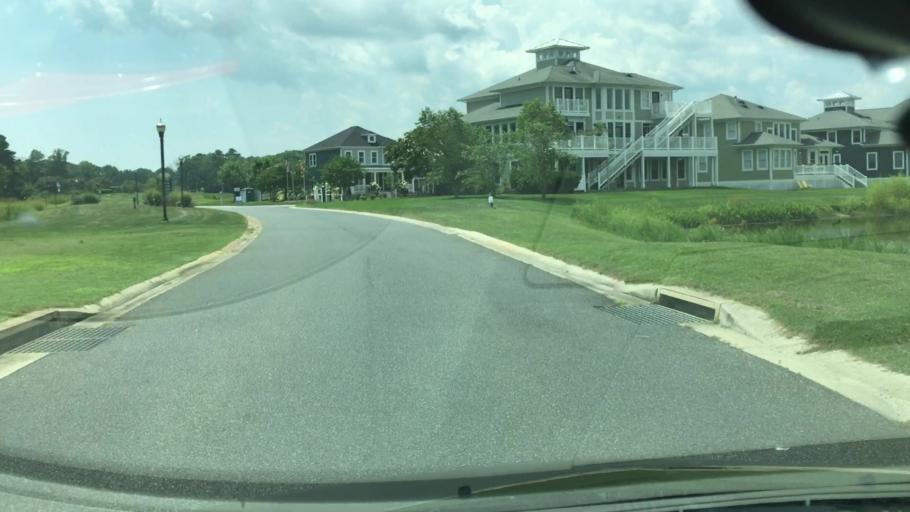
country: US
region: Maryland
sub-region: Worcester County
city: West Ocean City
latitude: 38.3449
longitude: -75.1537
